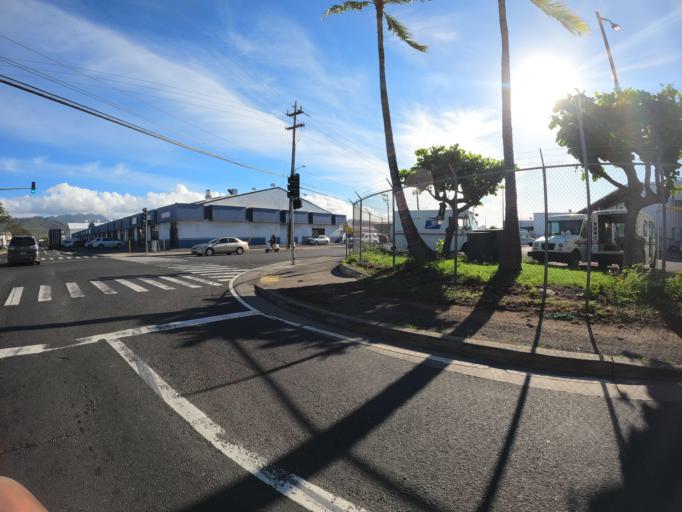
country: US
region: Hawaii
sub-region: Honolulu County
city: Honolulu
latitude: 21.3229
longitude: -157.8913
